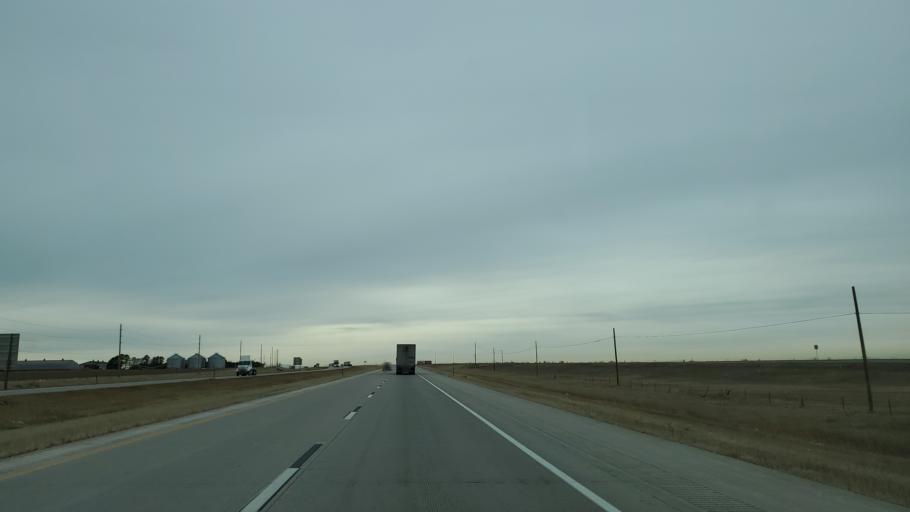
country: US
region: Colorado
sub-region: Adams County
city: Bennett
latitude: 39.7404
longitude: -104.6220
